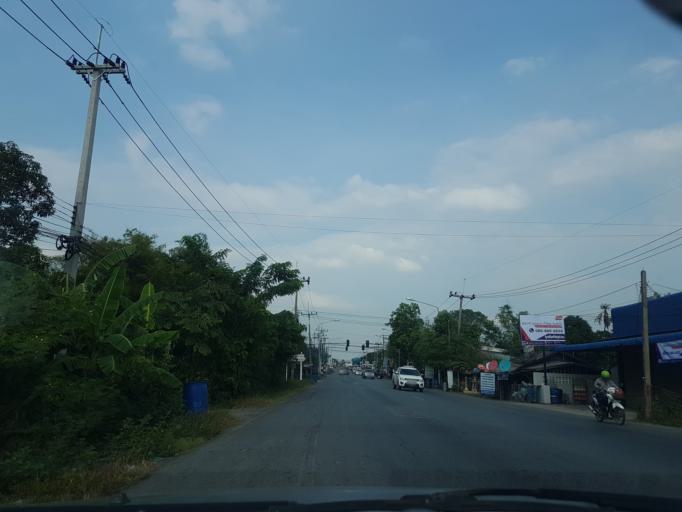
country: TH
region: Sara Buri
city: Ban Mo
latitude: 14.6058
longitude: 100.7374
